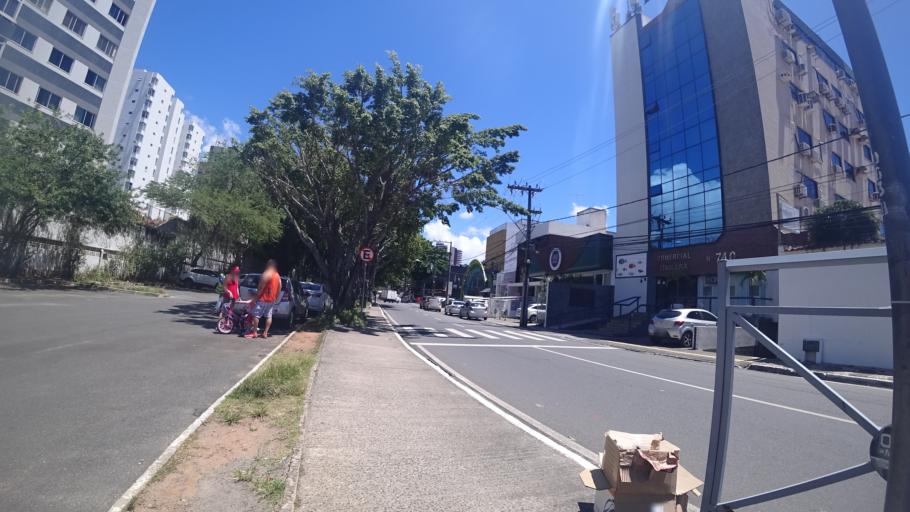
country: BR
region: Bahia
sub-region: Salvador
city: Salvador
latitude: -12.9926
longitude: -38.4613
